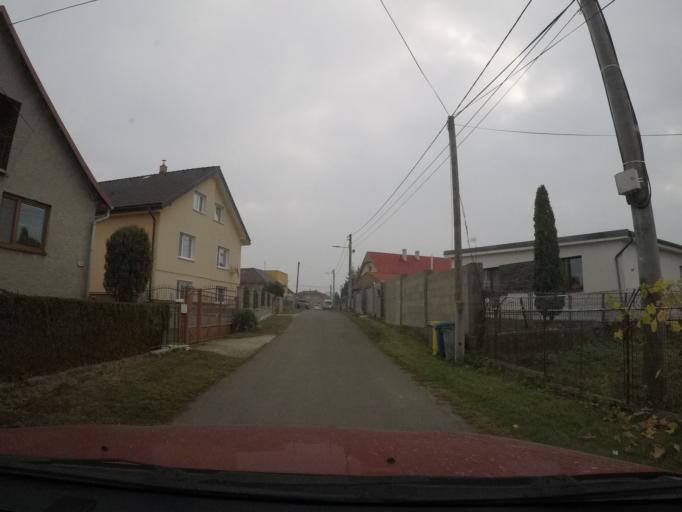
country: SK
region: Presovsky
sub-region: Okres Presov
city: Presov
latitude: 48.8713
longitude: 21.2682
